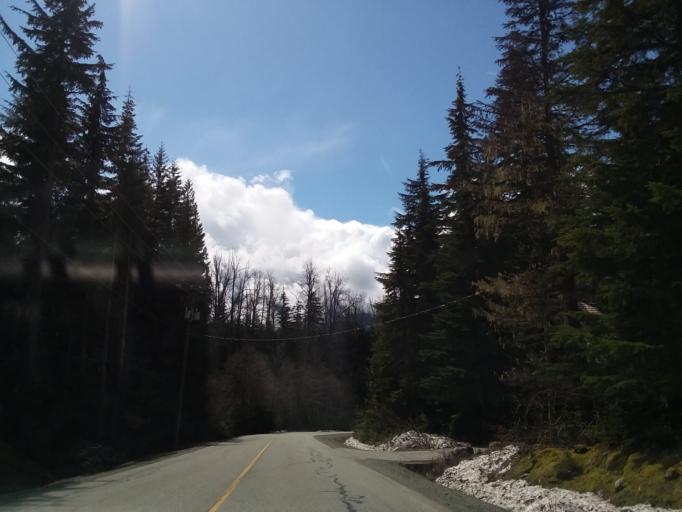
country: CA
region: British Columbia
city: Whistler
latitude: 50.1283
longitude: -122.9862
